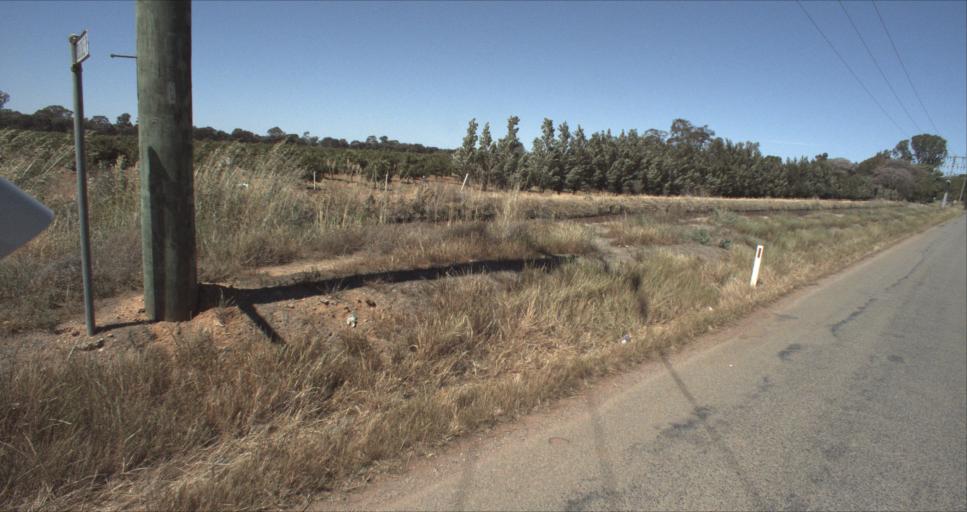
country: AU
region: New South Wales
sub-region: Leeton
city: Leeton
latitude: -34.5470
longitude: 146.3696
